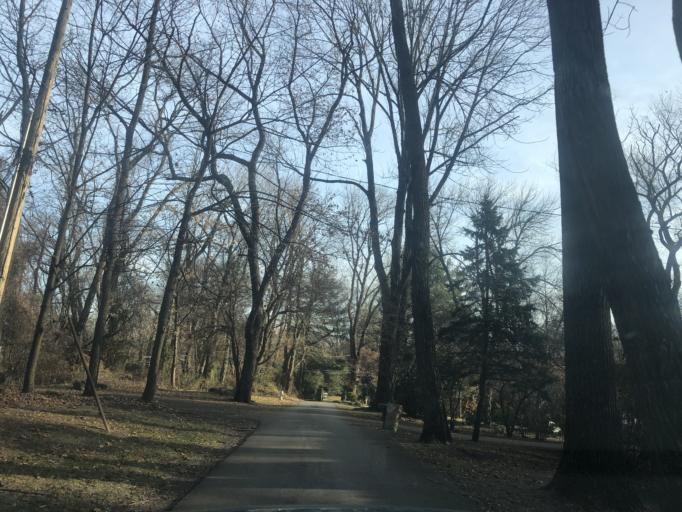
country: US
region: Pennsylvania
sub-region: Delaware County
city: Radnor
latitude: 40.0367
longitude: -75.3649
